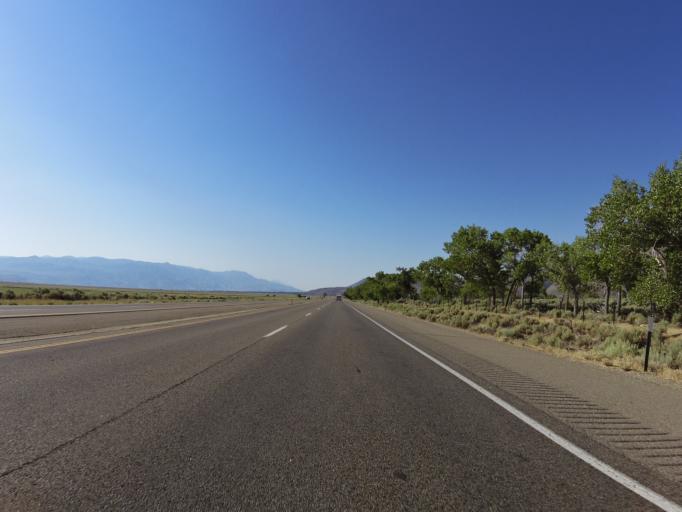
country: US
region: California
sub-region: Inyo County
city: Big Pine
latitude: 37.2418
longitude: -118.3525
